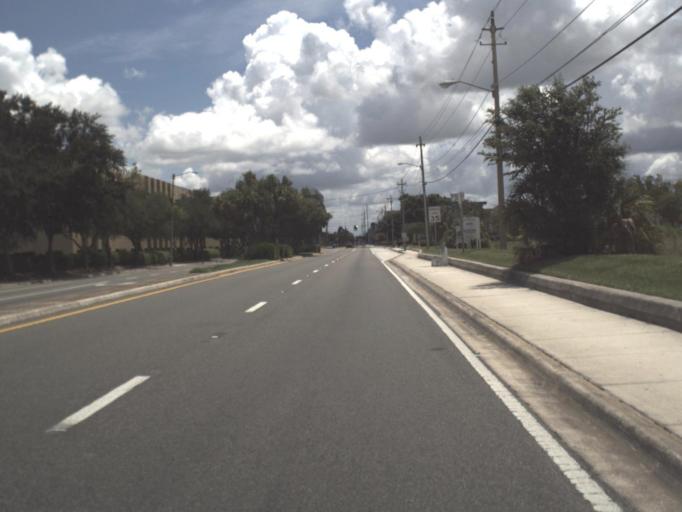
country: US
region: Florida
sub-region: Hillsborough County
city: Egypt Lake-Leto
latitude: 27.9813
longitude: -82.5011
